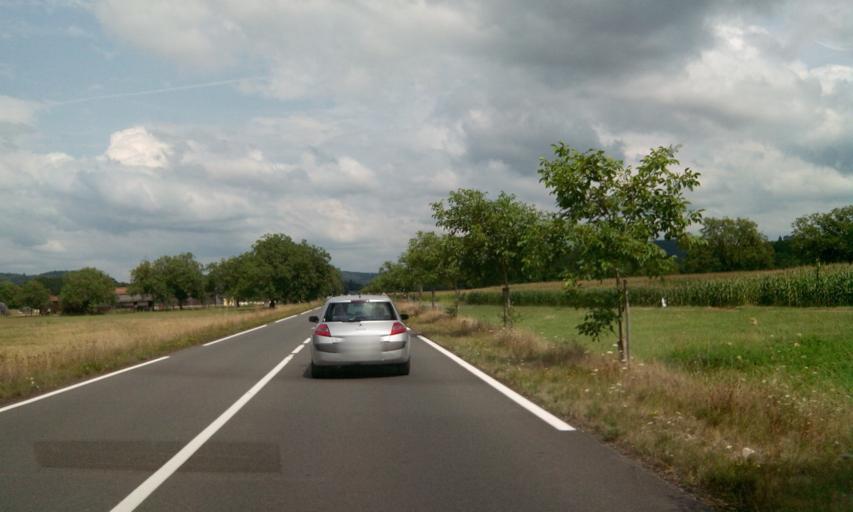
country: FR
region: Aquitaine
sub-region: Departement de la Dordogne
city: Carsac-Aillac
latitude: 44.8486
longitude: 1.3143
